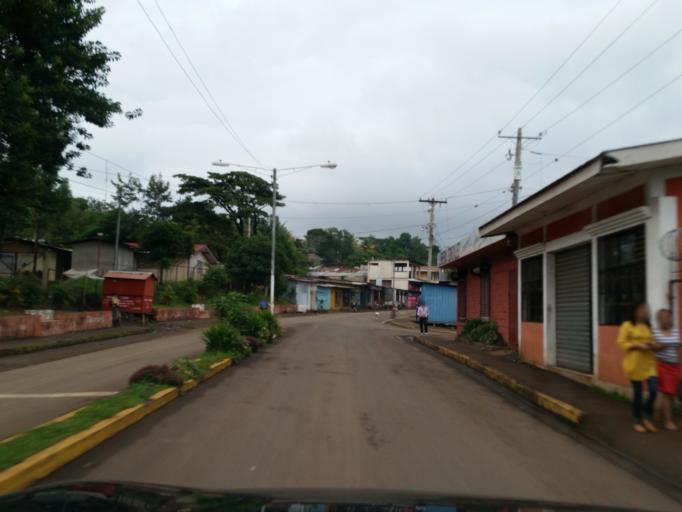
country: NI
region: Matagalpa
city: San Ramon
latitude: 13.1362
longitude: -85.7363
